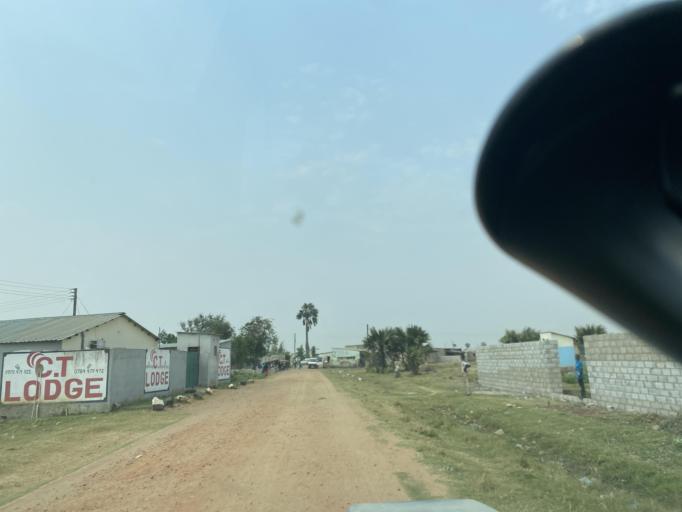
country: ZM
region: Lusaka
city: Kafue
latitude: -15.6883
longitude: 28.0074
